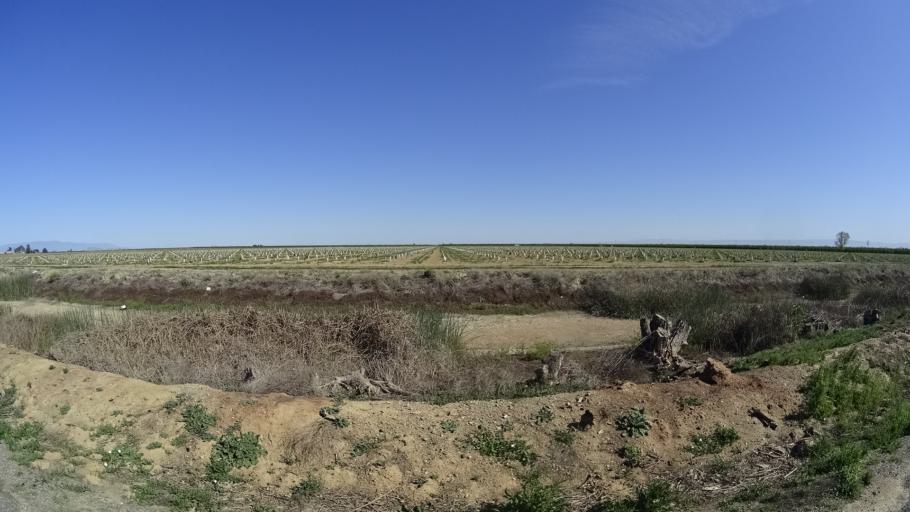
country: US
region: California
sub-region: Glenn County
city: Willows
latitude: 39.6112
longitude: -122.1412
